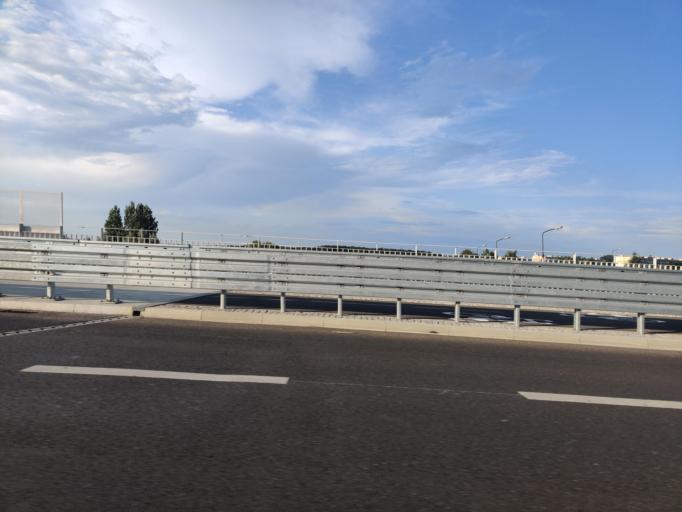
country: PL
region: Greater Poland Voivodeship
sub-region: Konin
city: Konin
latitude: 52.2341
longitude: 18.2730
